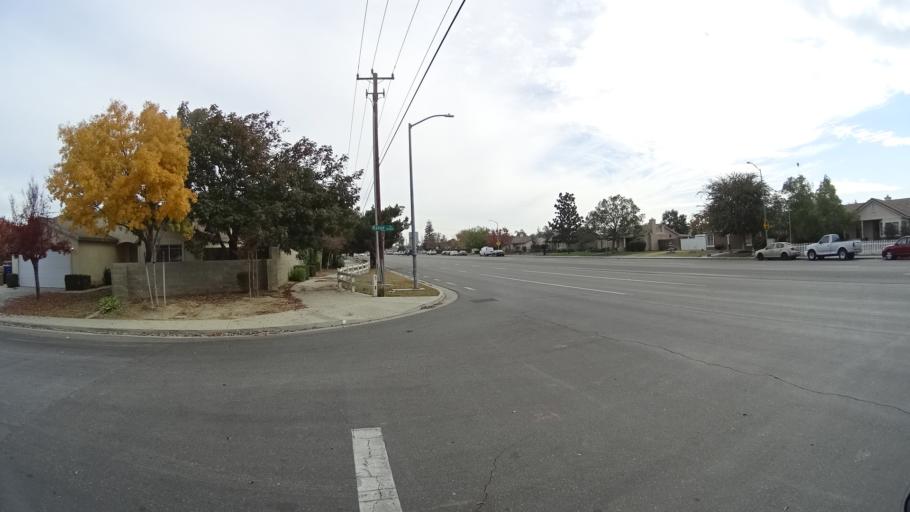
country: US
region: California
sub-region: Kern County
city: Rosedale
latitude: 35.3981
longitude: -119.1305
